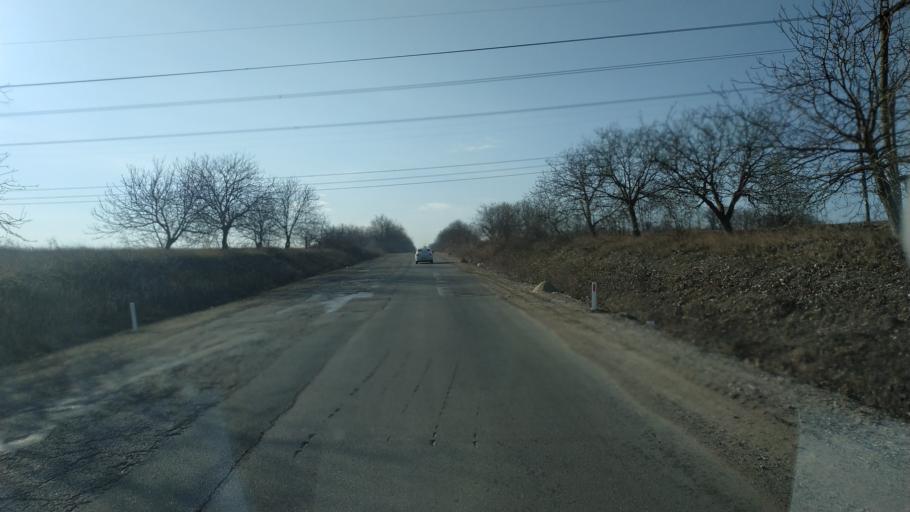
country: MD
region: Chisinau
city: Singera
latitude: 46.8743
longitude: 29.0396
